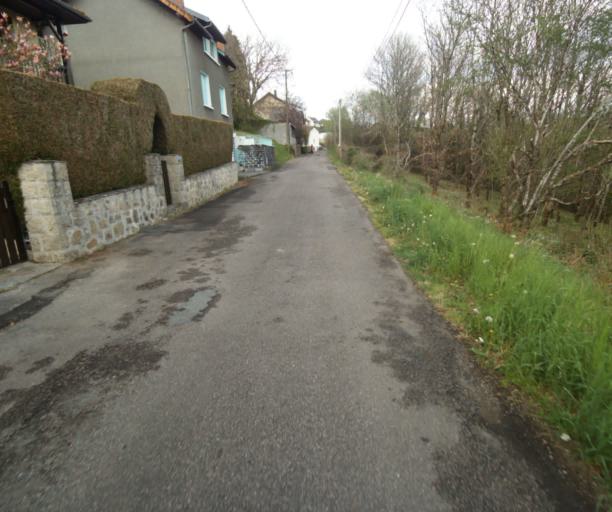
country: FR
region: Limousin
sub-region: Departement de la Correze
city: Tulle
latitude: 45.2556
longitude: 1.7402
